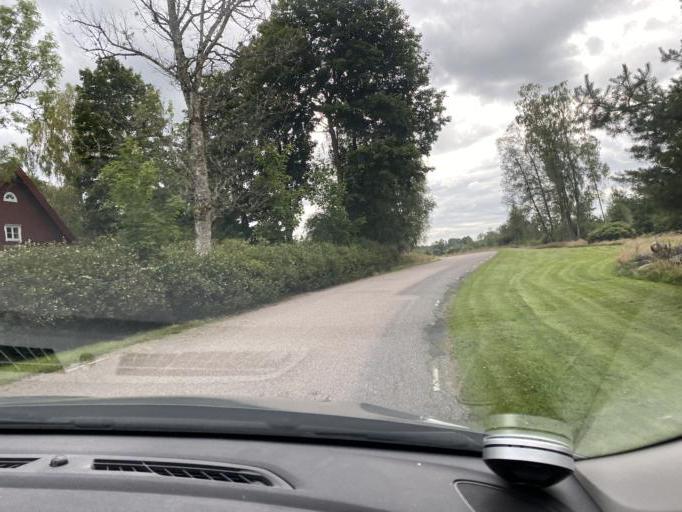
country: SE
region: Kronoberg
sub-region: Markaryds Kommun
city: Markaryd
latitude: 56.4758
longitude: 13.5653
